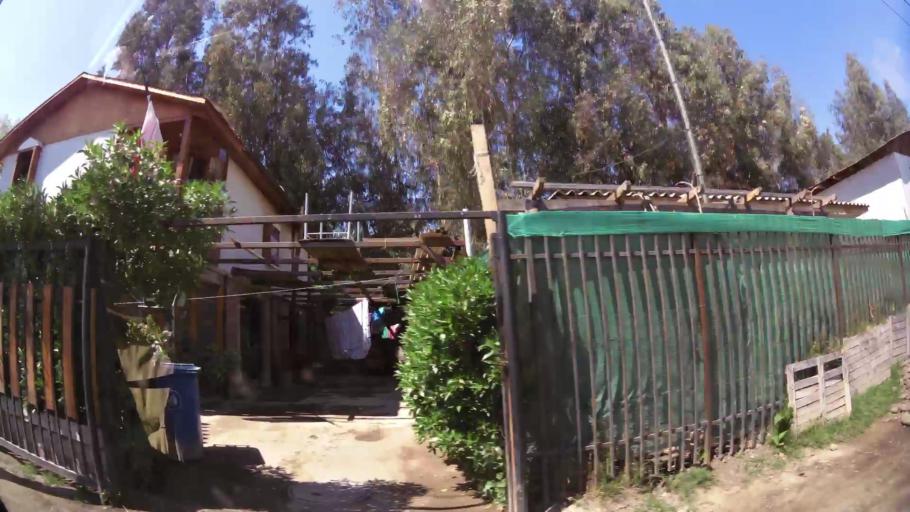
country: CL
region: Santiago Metropolitan
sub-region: Provincia de Talagante
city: Penaflor
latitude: -33.5859
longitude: -70.8050
